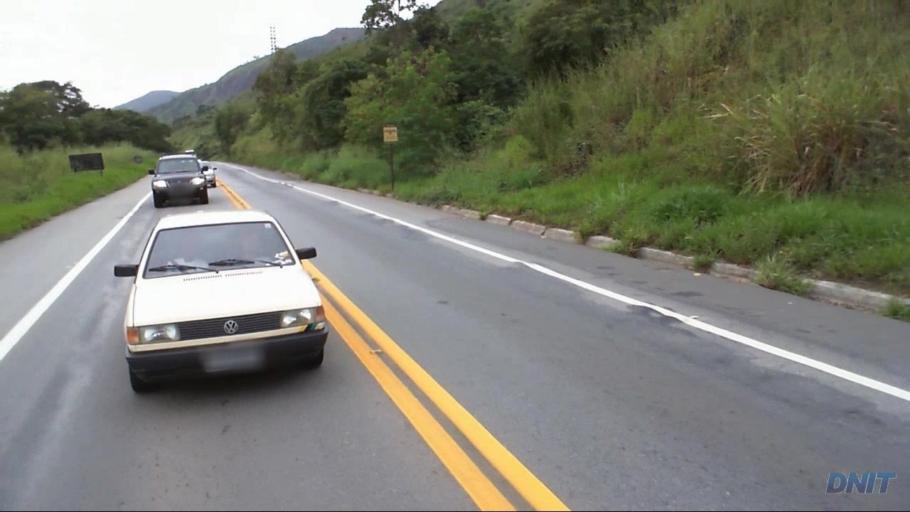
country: BR
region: Minas Gerais
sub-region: Timoteo
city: Timoteo
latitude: -19.5934
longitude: -42.7401
